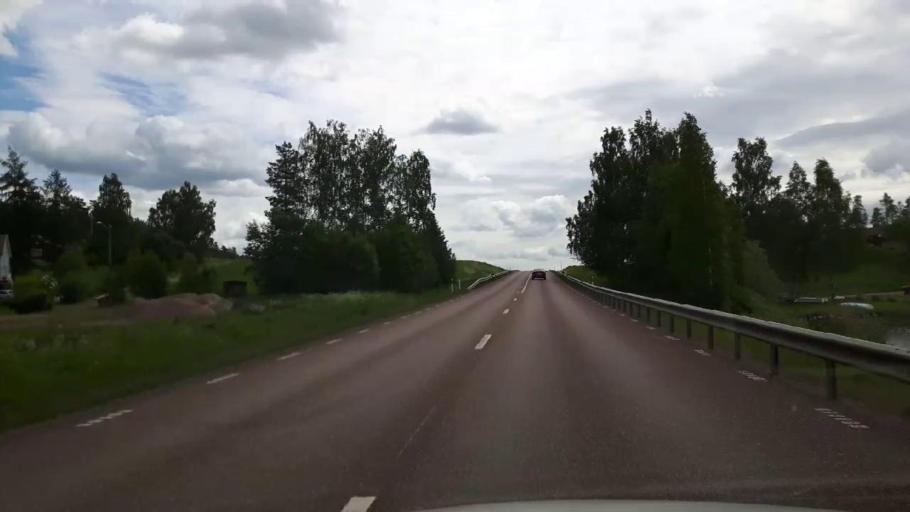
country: SE
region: Dalarna
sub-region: Hedemora Kommun
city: Hedemora
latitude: 60.3221
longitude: 15.9546
